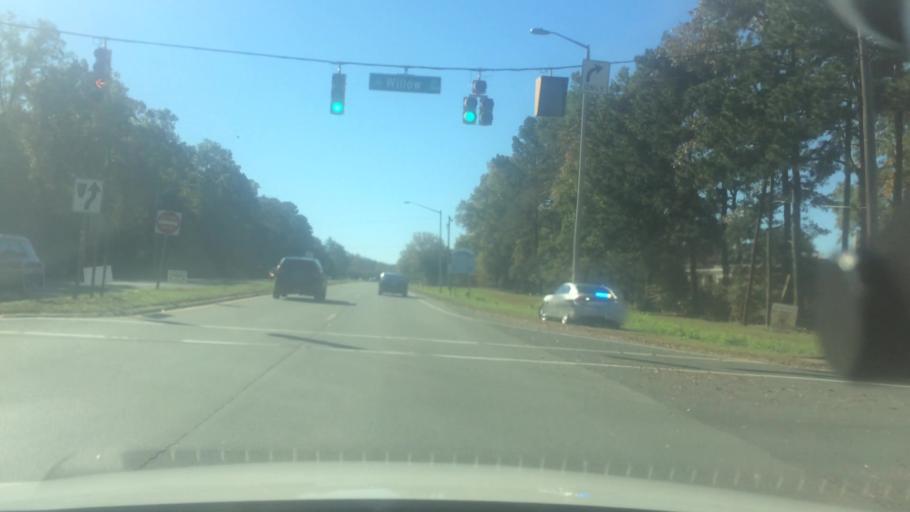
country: US
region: North Carolina
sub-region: Orange County
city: Chapel Hill
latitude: 35.9304
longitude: -79.0243
